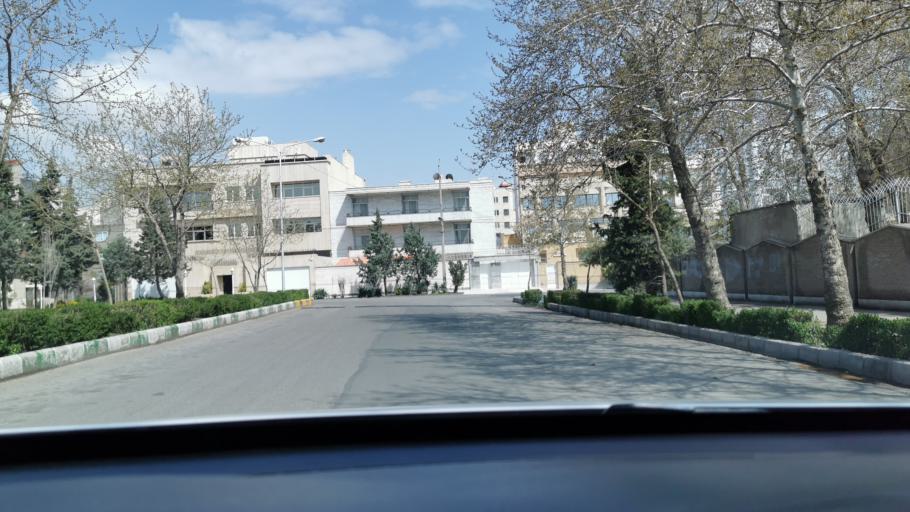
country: IR
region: Razavi Khorasan
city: Mashhad
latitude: 36.3202
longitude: 59.5309
